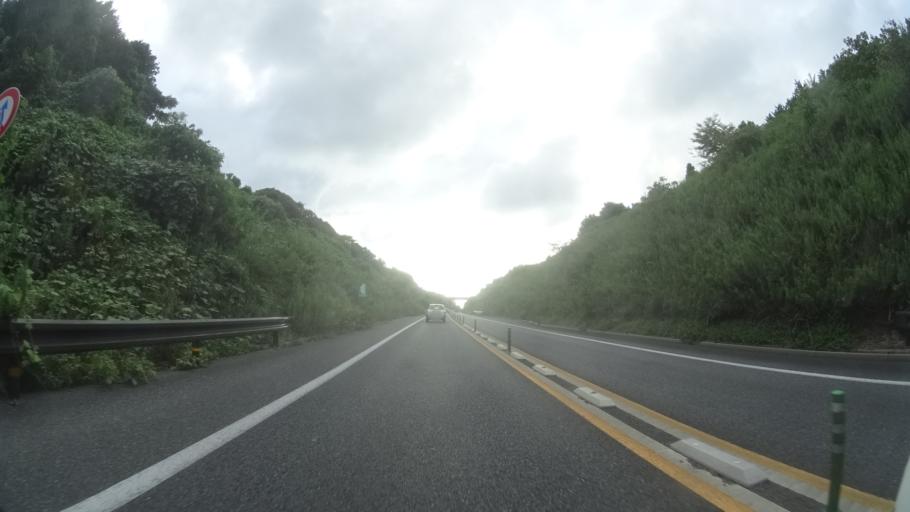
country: JP
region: Tottori
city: Kurayoshi
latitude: 35.5073
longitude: 133.6134
